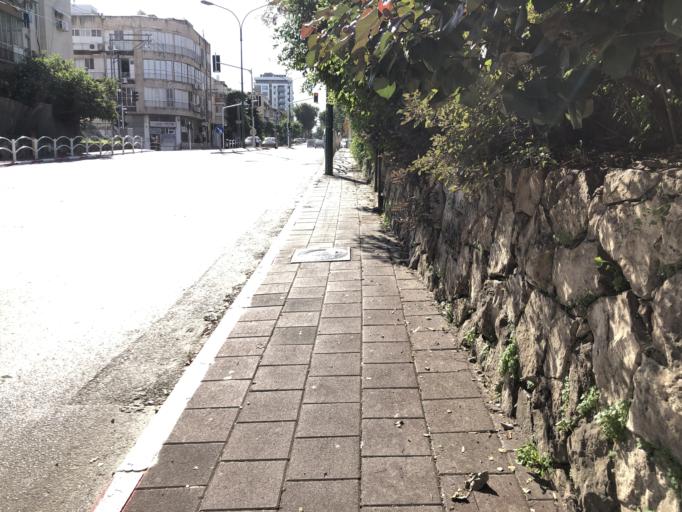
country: IL
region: Tel Aviv
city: Bene Beraq
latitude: 32.0751
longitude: 34.8251
